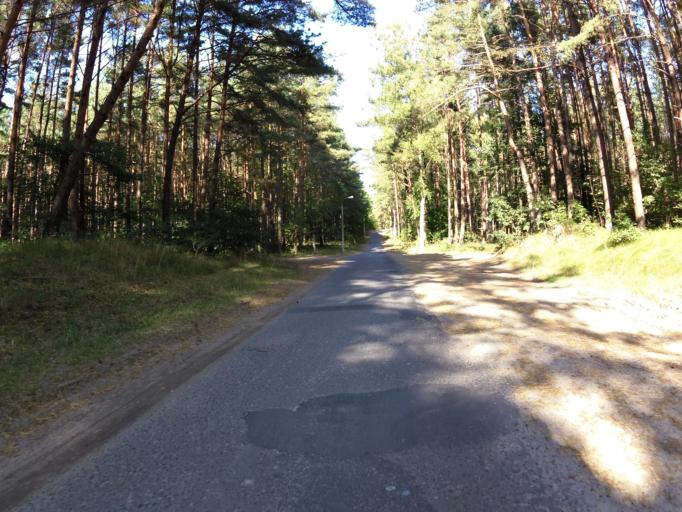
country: DE
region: Mecklenburg-Vorpommern
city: Seebad Heringsdorf
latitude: 53.9319
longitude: 14.2015
